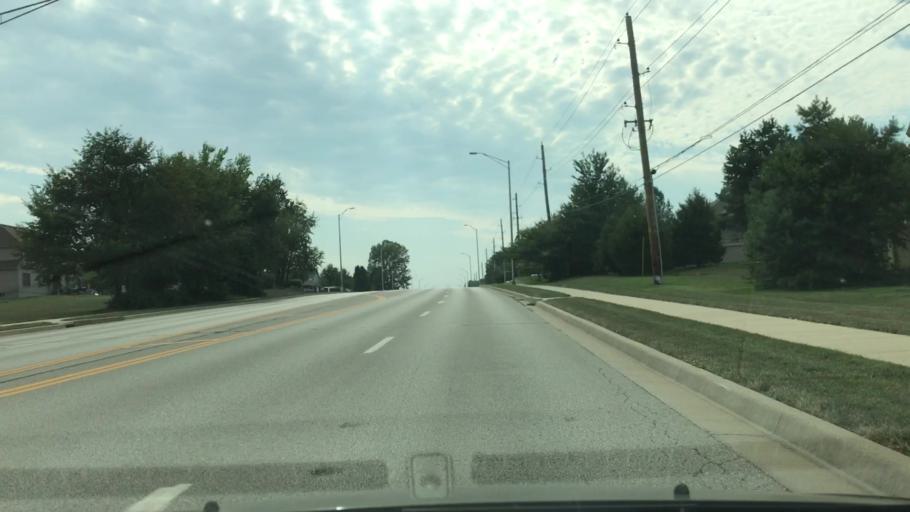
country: US
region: Missouri
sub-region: Jackson County
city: Lees Summit
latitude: 38.9128
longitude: -94.4387
